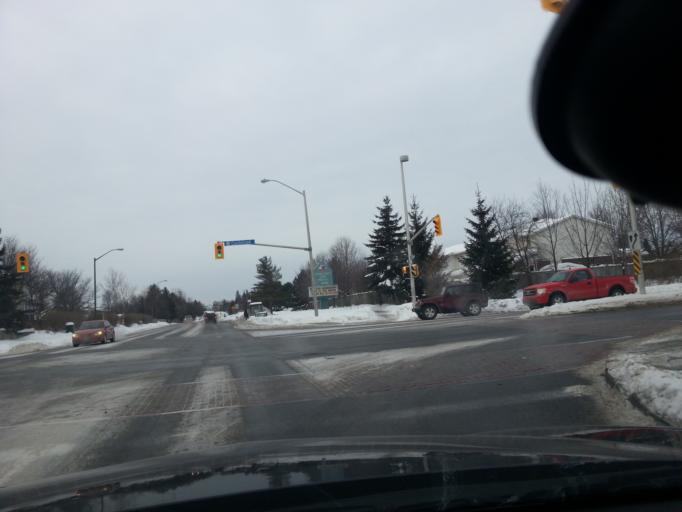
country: CA
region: Ontario
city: Bells Corners
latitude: 45.3091
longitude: -75.8985
